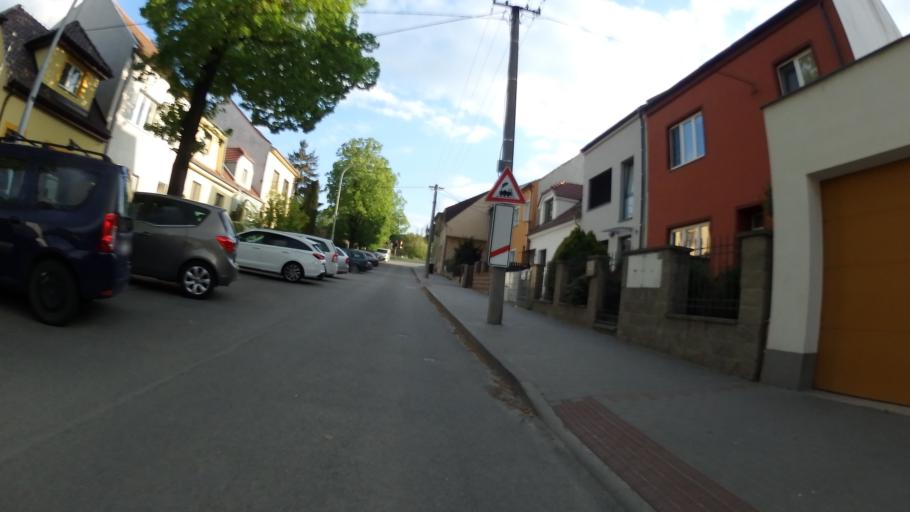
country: CZ
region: South Moravian
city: Ostopovice
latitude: 49.1629
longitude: 16.5646
